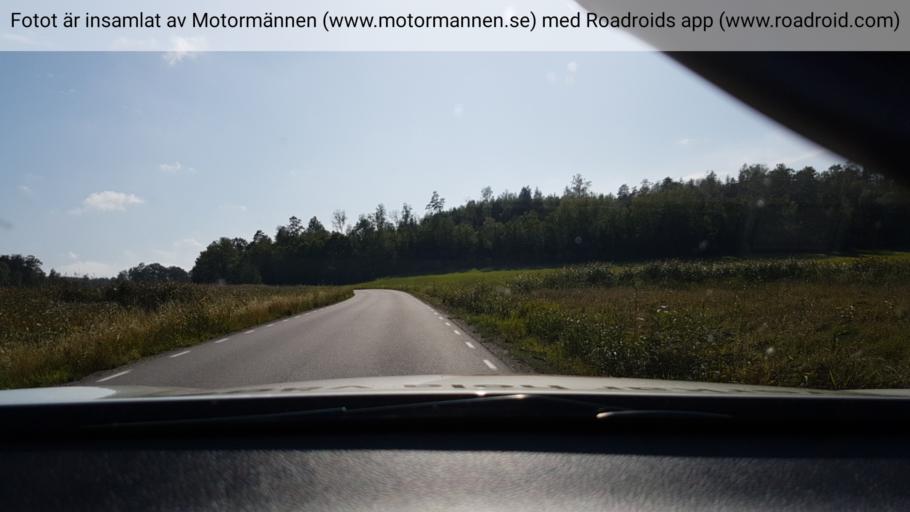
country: SE
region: Stockholm
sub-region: Nynashamns Kommun
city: Osmo
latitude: 58.9107
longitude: 17.8517
